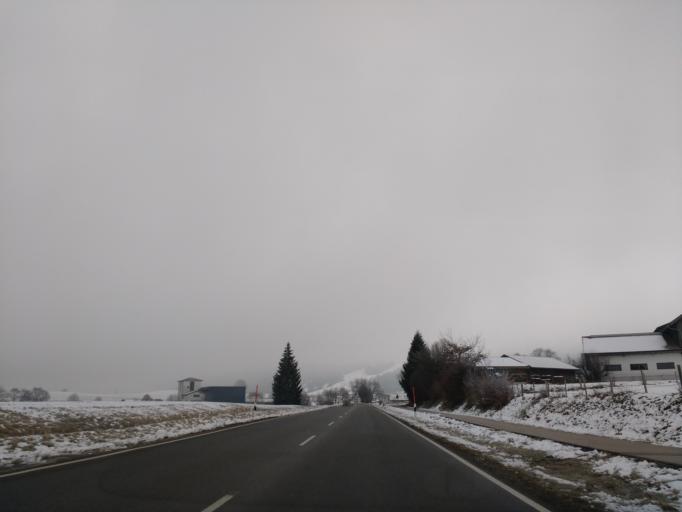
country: DE
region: Bavaria
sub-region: Swabia
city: Nesselwang
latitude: 47.6302
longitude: 10.4835
